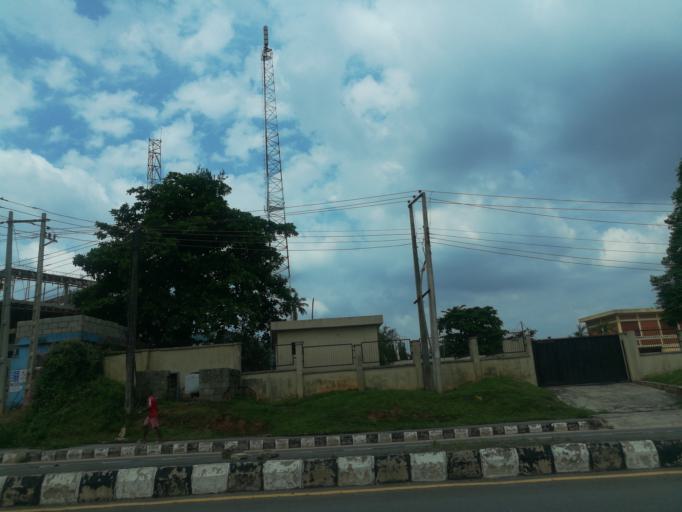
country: NG
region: Oyo
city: Ibadan
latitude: 7.3969
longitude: 3.8773
